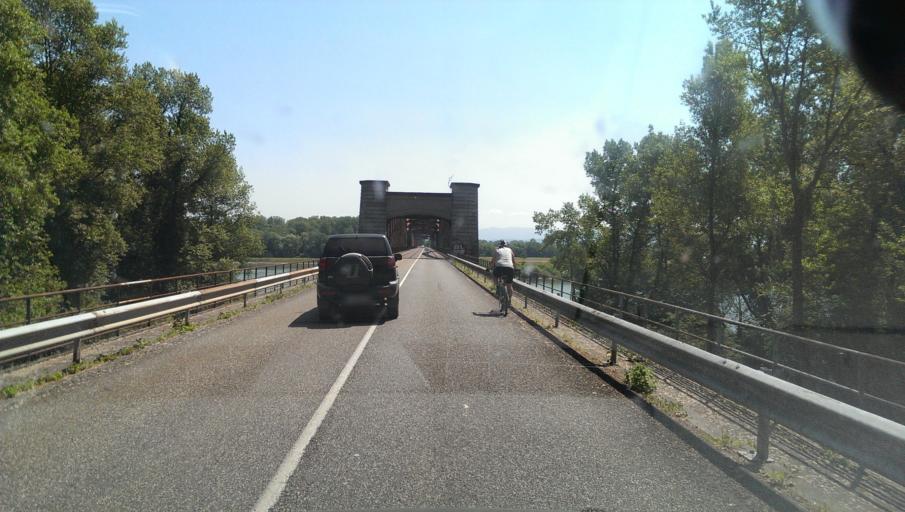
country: DE
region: Baden-Wuerttemberg
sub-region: Karlsruhe Region
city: Iffezheim
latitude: 48.8484
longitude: 8.1104
